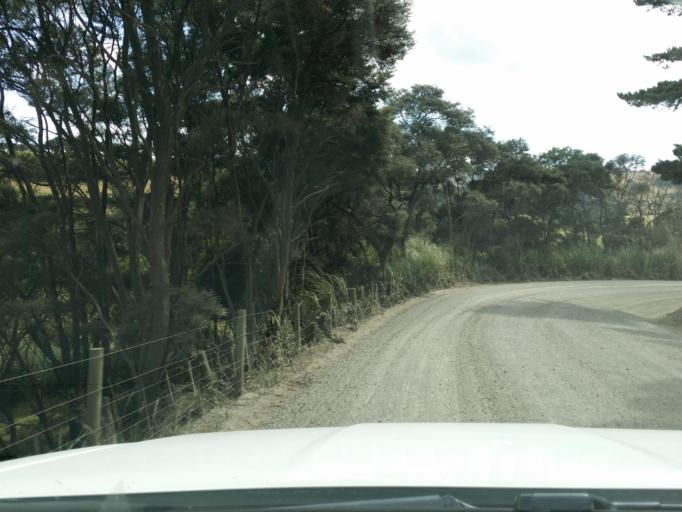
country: NZ
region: Auckland
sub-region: Auckland
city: Wellsford
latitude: -36.3008
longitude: 174.1088
